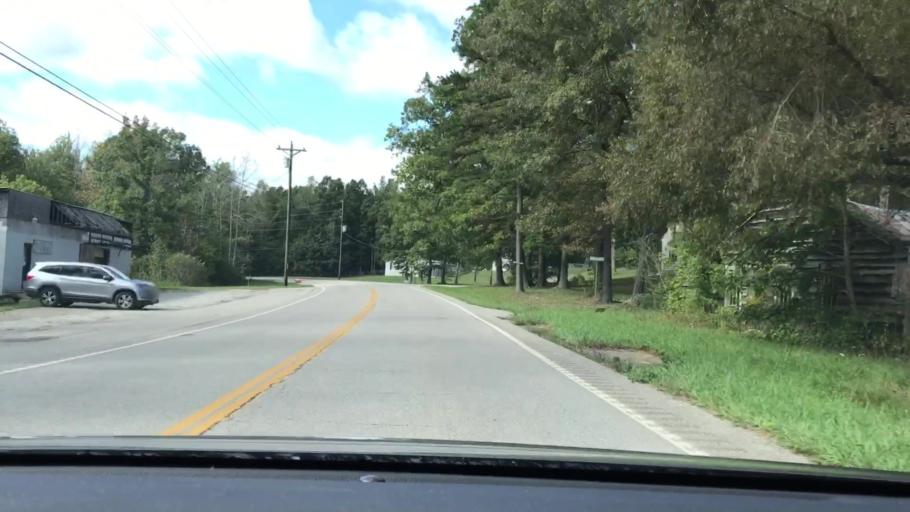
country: US
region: Tennessee
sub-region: Scott County
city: Huntsville
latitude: 36.3373
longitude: -84.6107
